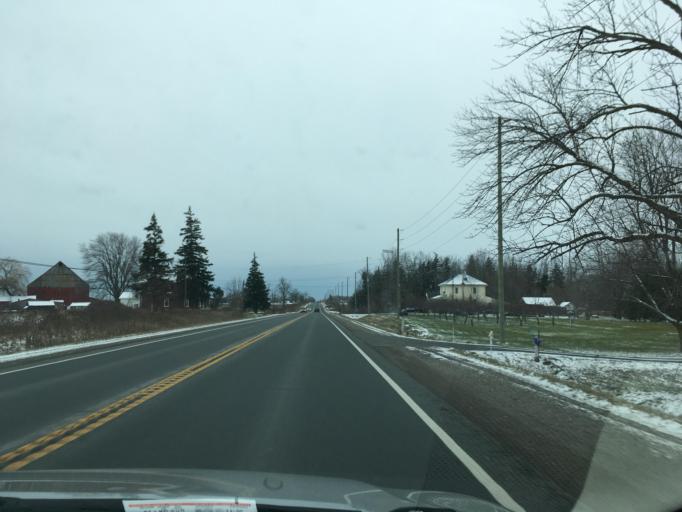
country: CA
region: Ontario
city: Brantford
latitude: 42.9358
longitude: -80.0755
